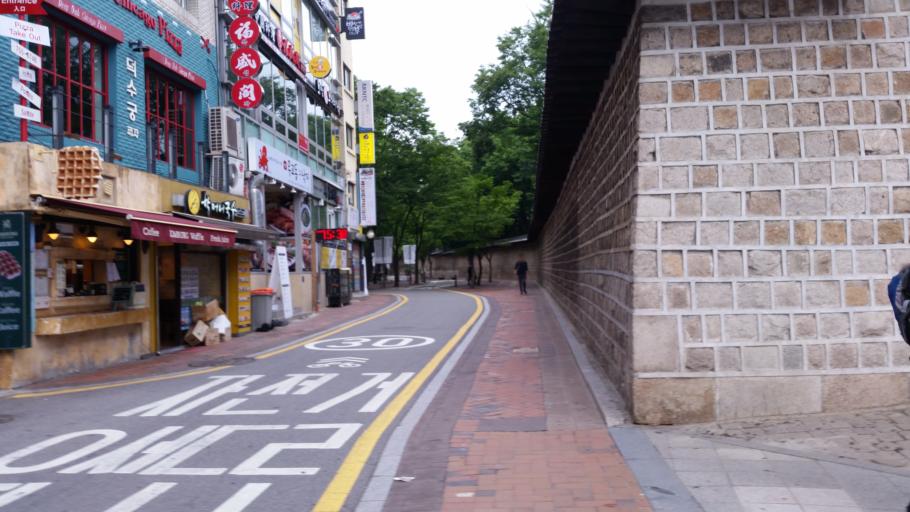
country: KR
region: Seoul
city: Seoul
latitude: 37.5648
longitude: 126.9767
